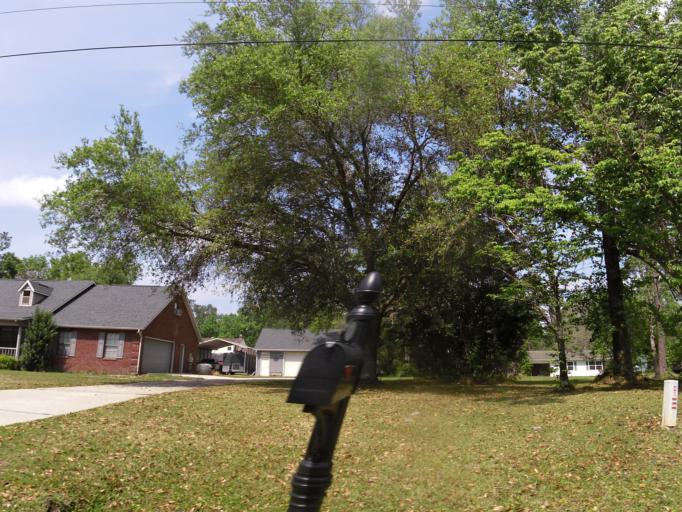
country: US
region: Georgia
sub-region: Camden County
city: Kingsland
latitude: 30.7837
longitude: -81.6980
